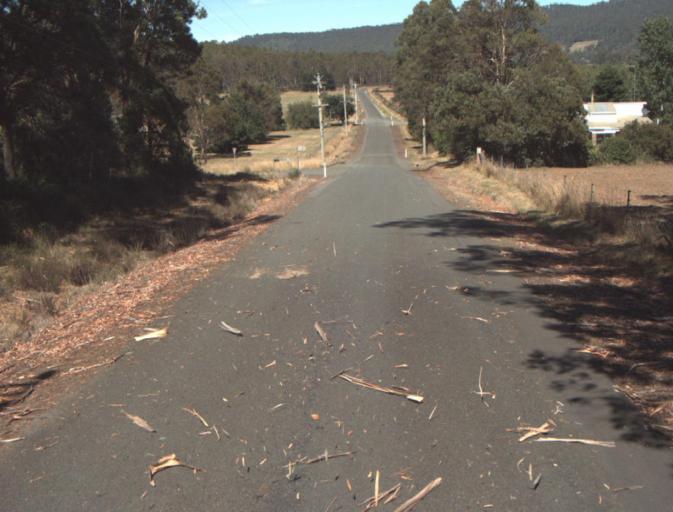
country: AU
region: Tasmania
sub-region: Launceston
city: Newstead
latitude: -41.3208
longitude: 147.3229
